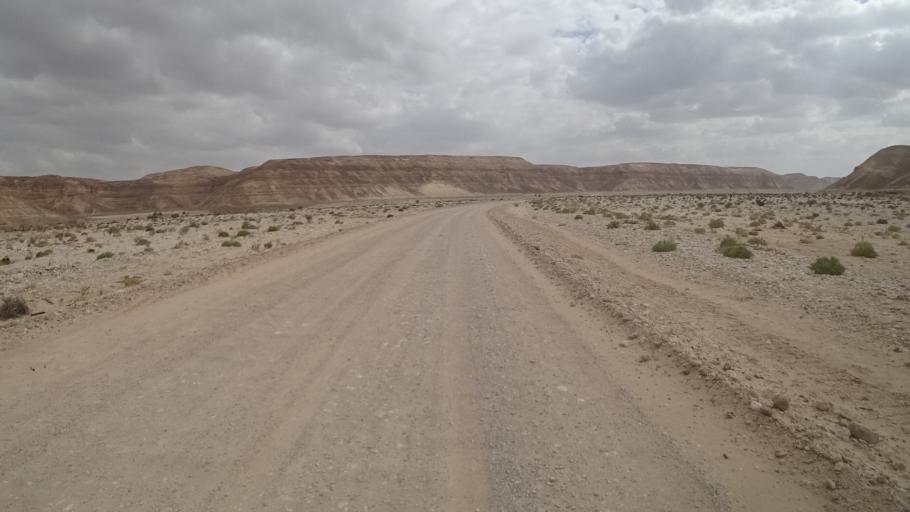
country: YE
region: Al Mahrah
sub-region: Shahan
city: Shihan as Sufla
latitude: 17.4692
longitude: 53.0041
